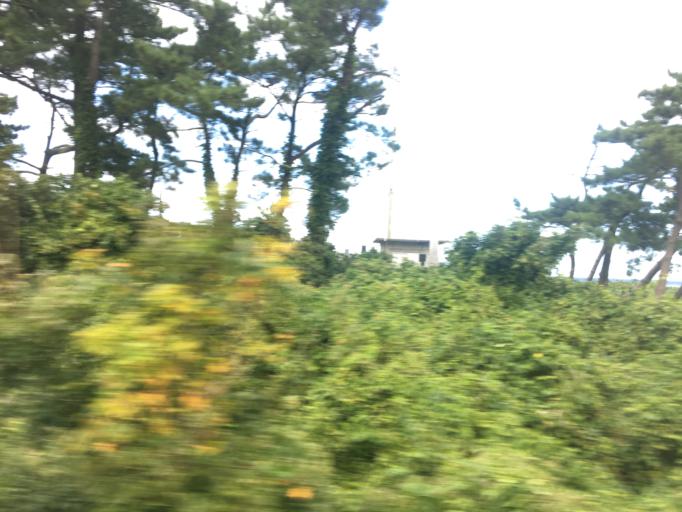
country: JP
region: Aomori
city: Shimokizukuri
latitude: 40.7588
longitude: 140.1571
